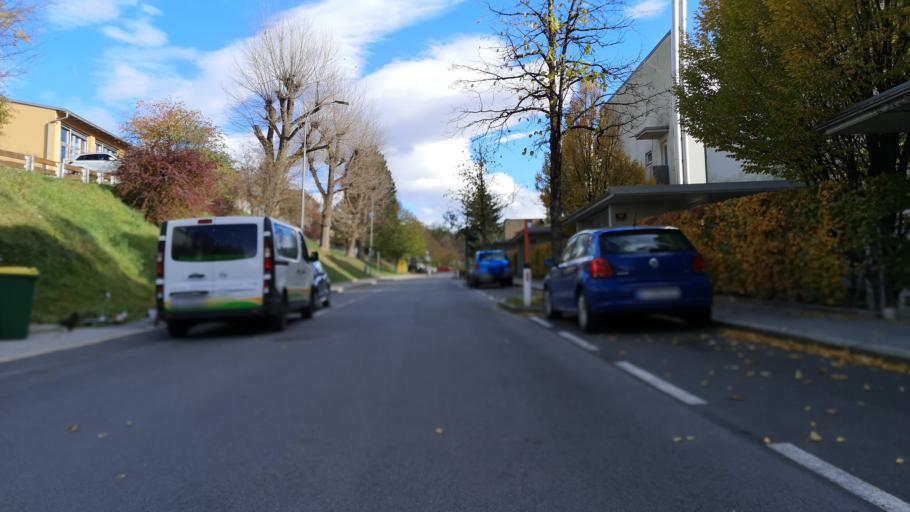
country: AT
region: Tyrol
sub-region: Politischer Bezirk Innsbruck Land
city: Vols
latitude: 47.2671
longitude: 11.3557
